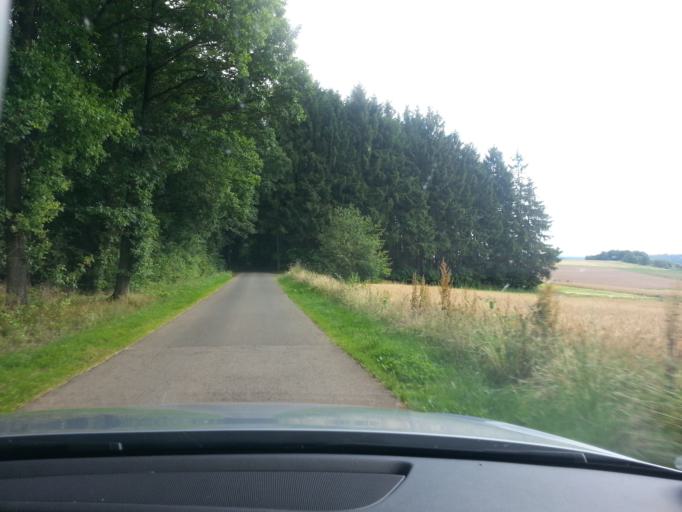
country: DE
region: Saarland
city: Marpingen
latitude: 49.4435
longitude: 7.0929
